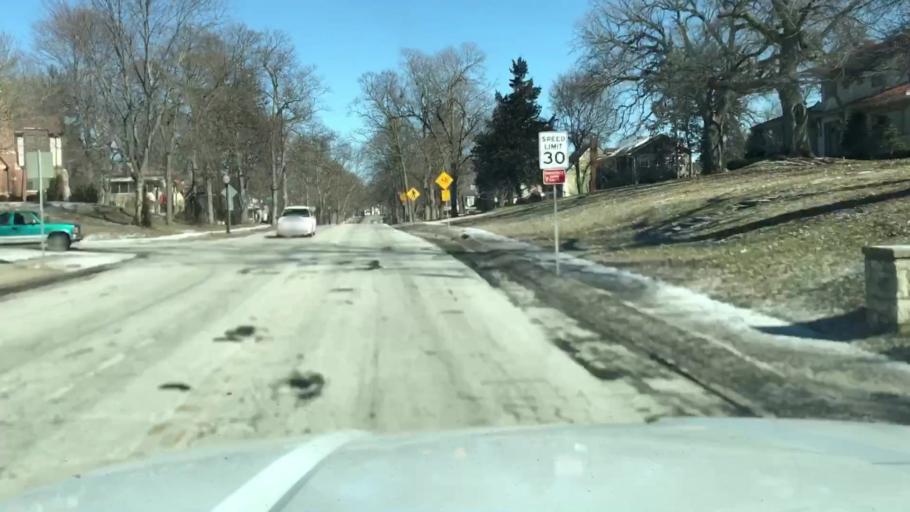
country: US
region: Missouri
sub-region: Buchanan County
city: Saint Joseph
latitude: 39.7807
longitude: -94.8251
